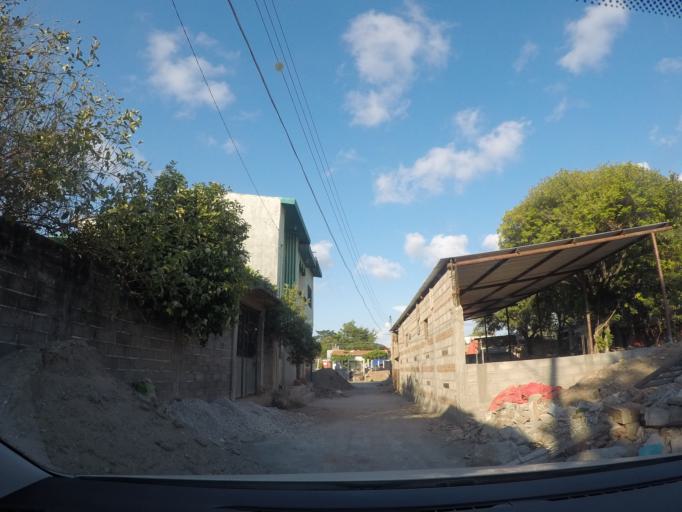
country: MX
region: Oaxaca
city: Juchitan de Zaragoza
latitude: 16.4355
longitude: -95.0285
